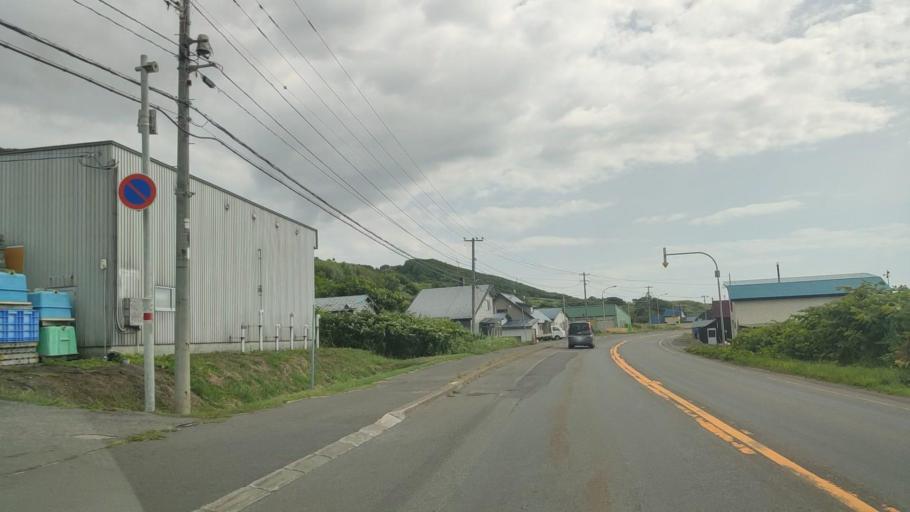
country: JP
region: Hokkaido
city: Rumoi
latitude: 44.1446
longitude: 141.6548
